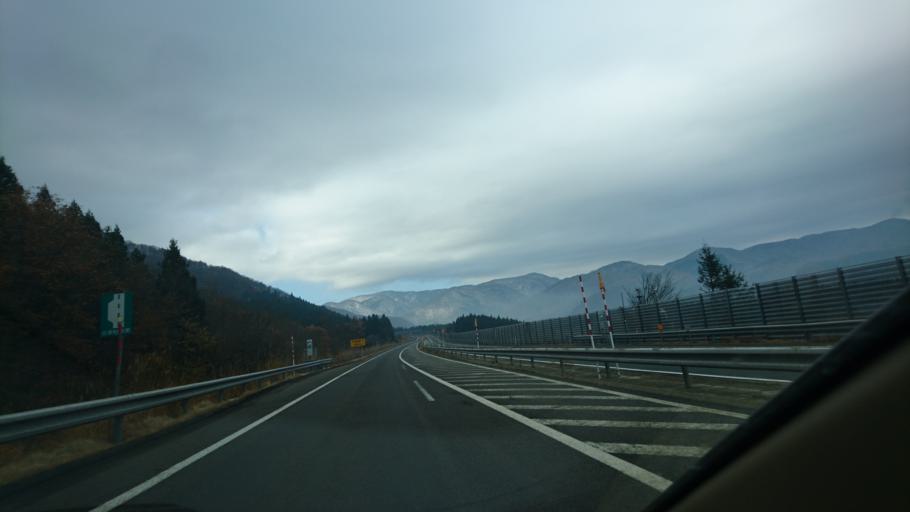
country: JP
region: Iwate
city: Kitakami
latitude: 39.2952
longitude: 140.9458
